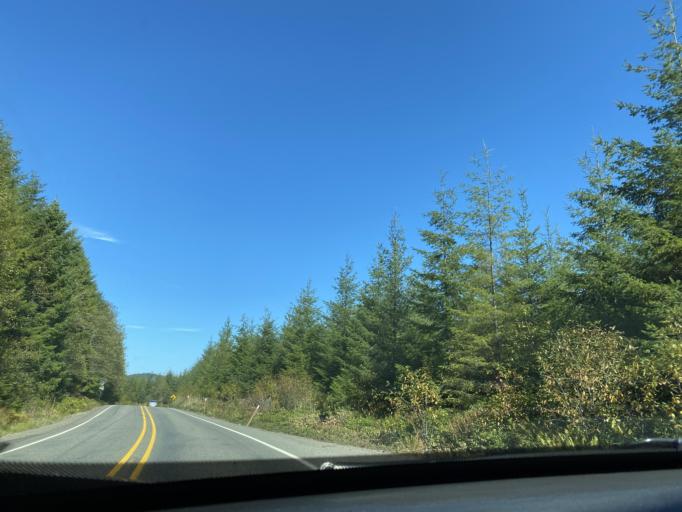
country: US
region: Washington
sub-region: Clallam County
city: Forks
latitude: 47.9409
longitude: -124.4630
